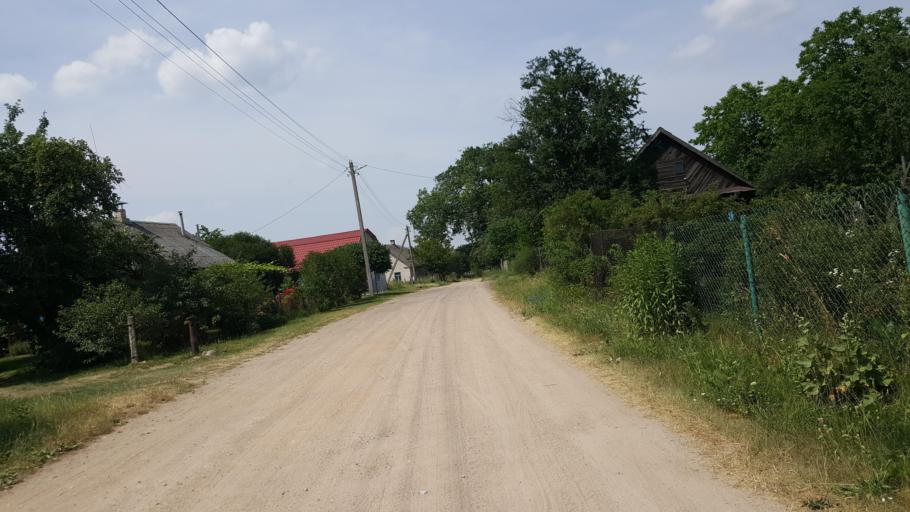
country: BY
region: Brest
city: Kamyanyets
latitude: 52.3302
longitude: 23.7777
